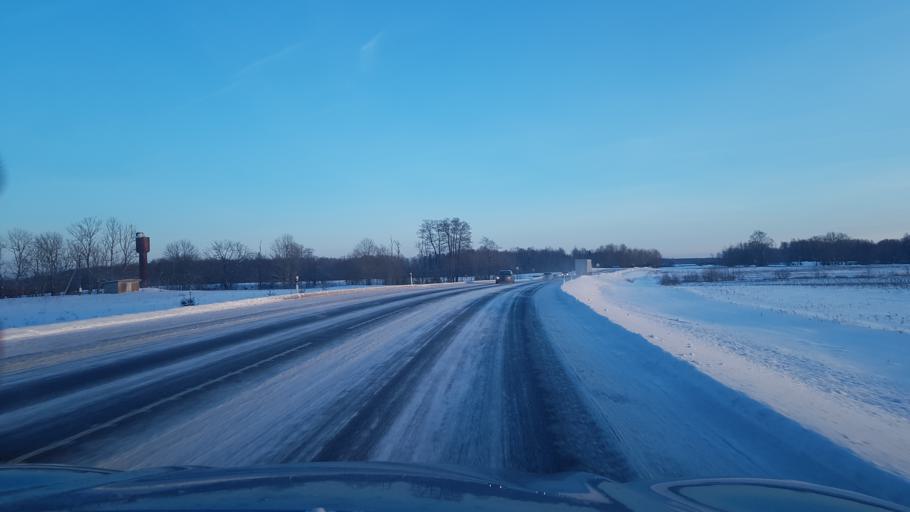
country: EE
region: Ida-Virumaa
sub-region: Narva-Joesuu linn
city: Narva-Joesuu
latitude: 59.3991
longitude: 28.0729
